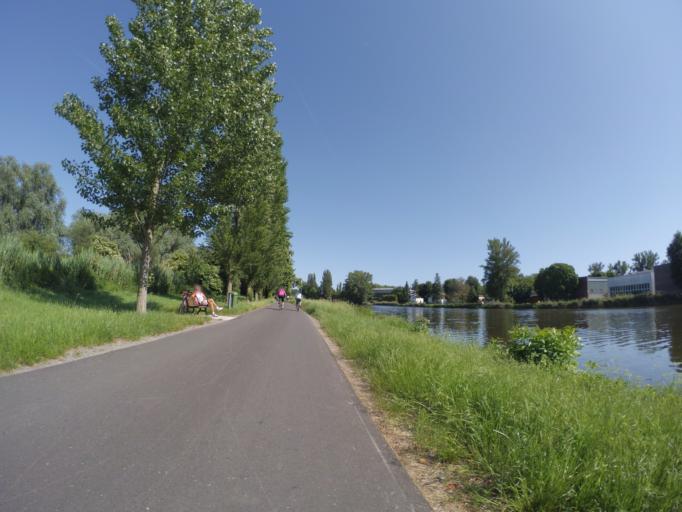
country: CZ
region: Central Bohemia
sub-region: Okres Nymburk
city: Nymburk
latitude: 50.1806
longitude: 15.0587
